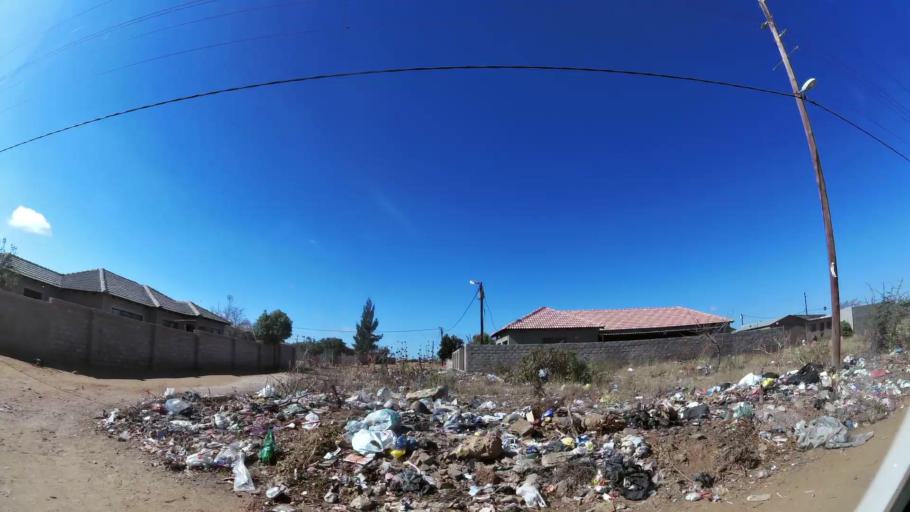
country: ZA
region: Limpopo
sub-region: Capricorn District Municipality
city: Polokwane
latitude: -23.8829
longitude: 29.4031
